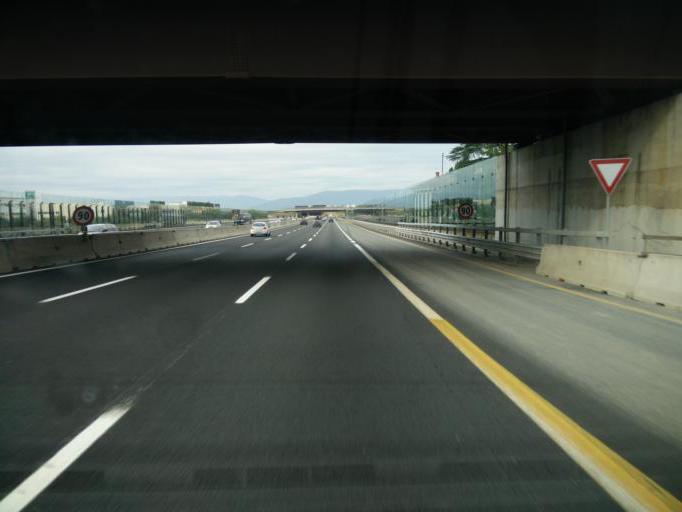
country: IT
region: Tuscany
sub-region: Province of Florence
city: Scandicci
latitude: 43.7557
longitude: 11.1709
